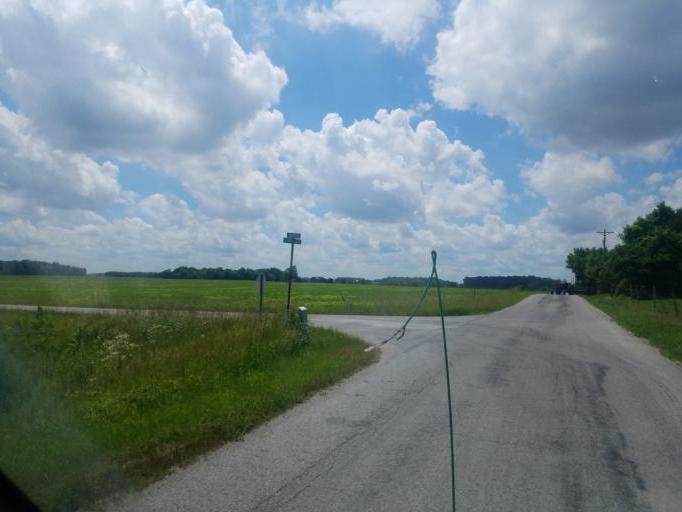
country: US
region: Ohio
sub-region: Huron County
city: Willard
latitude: 40.9967
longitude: -82.8346
